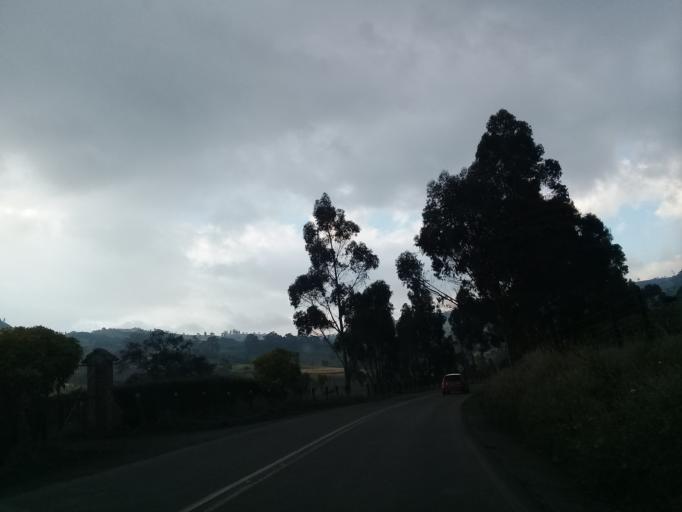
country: CO
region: Cundinamarca
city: Zipaquira
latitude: 5.0675
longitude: -74.0547
